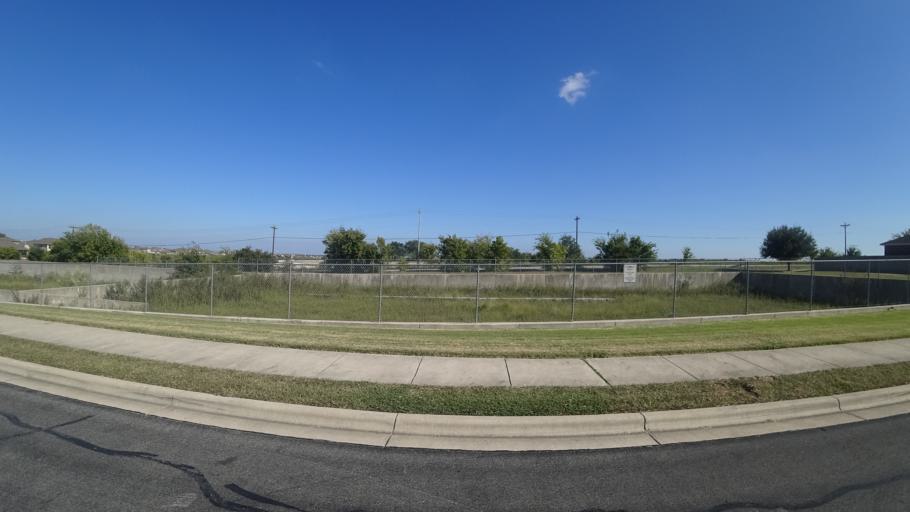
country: US
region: Texas
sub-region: Travis County
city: Manor
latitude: 30.3548
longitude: -97.6094
